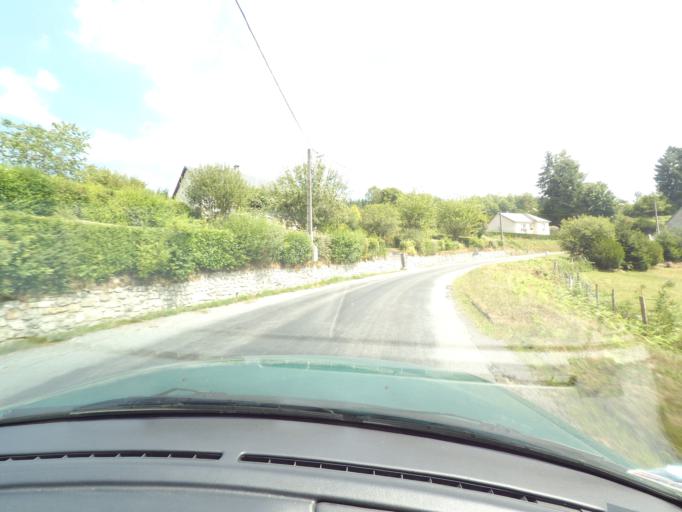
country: FR
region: Limousin
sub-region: Departement de la Correze
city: Bugeat
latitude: 45.7513
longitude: 1.9281
